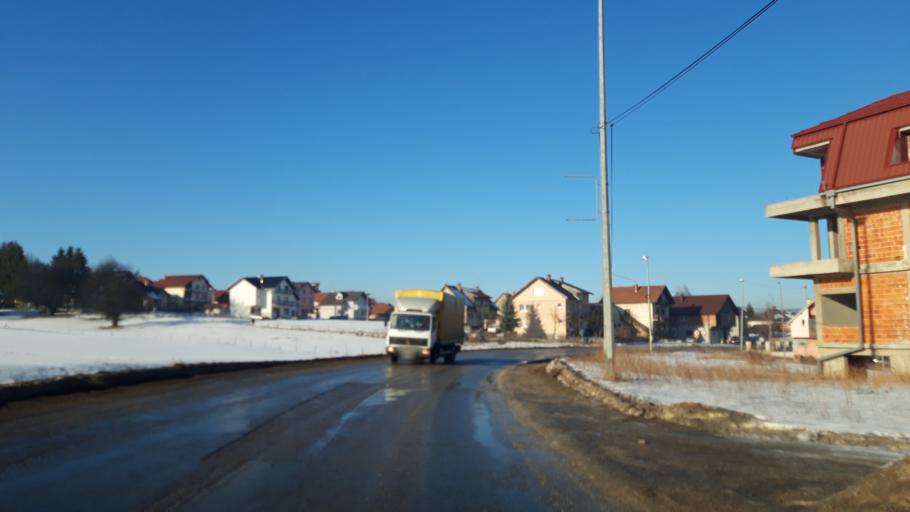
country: BA
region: Republika Srpska
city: Sokolac
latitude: 43.9328
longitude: 18.7901
